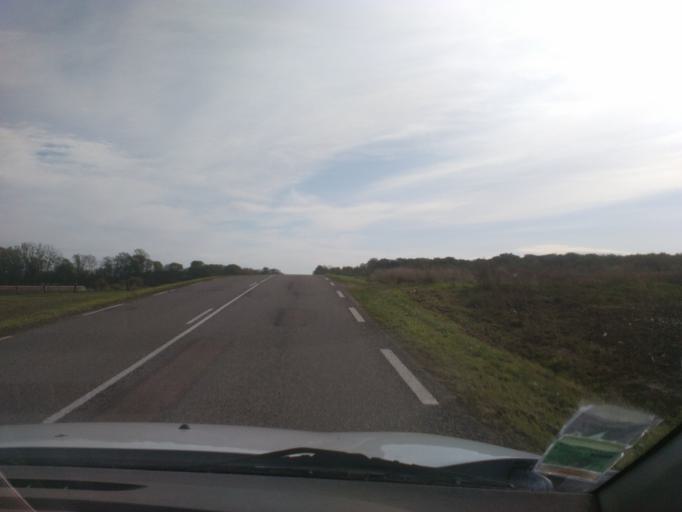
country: FR
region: Lorraine
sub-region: Departement des Vosges
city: Rambervillers
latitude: 48.3534
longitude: 6.6043
